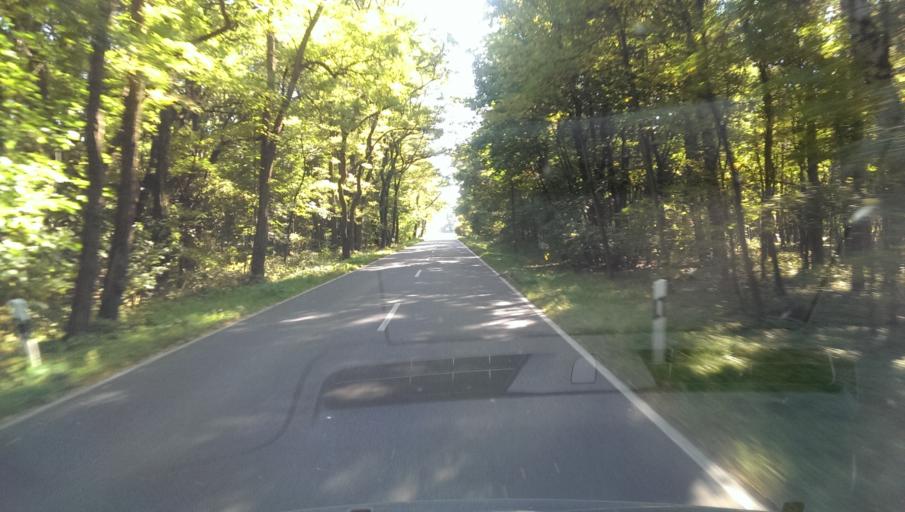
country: DE
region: Brandenburg
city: Halbe
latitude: 52.0335
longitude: 13.7186
